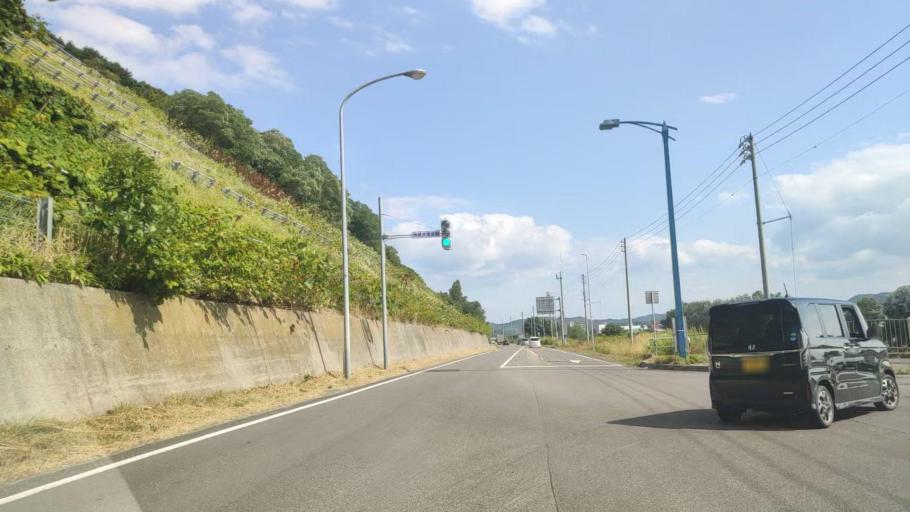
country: JP
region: Hokkaido
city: Rumoi
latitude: 43.9475
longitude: 141.6508
